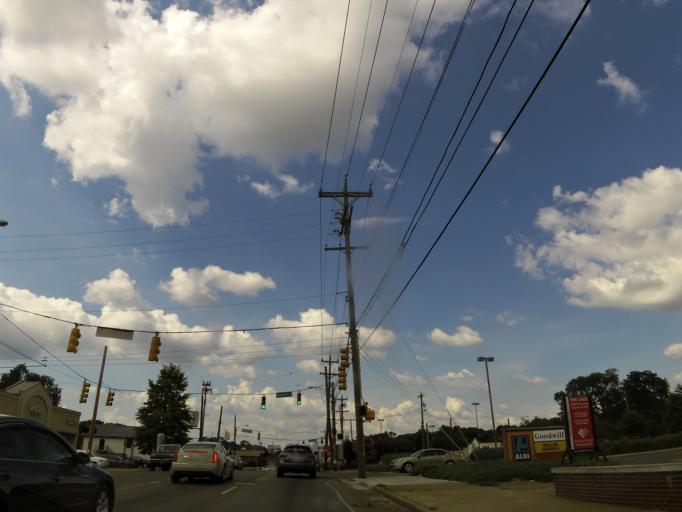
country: US
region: Tennessee
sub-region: Davidson County
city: Nashville
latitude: 36.1831
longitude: -86.7486
